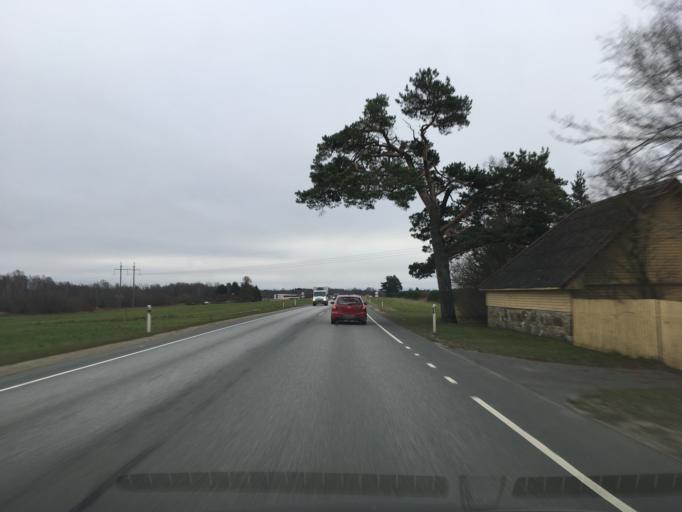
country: EE
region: Laeaene-Virumaa
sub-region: Someru vald
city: Someru
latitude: 59.3761
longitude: 26.4215
